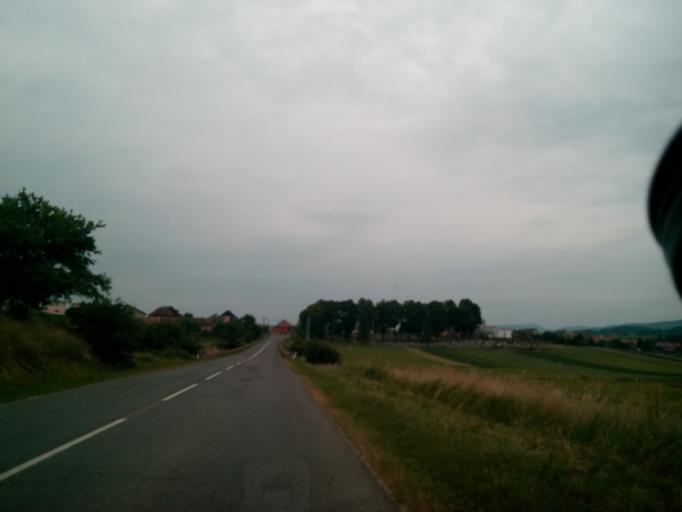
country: SK
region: Presovsky
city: Spisske Podhradie
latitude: 48.9461
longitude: 20.6992
